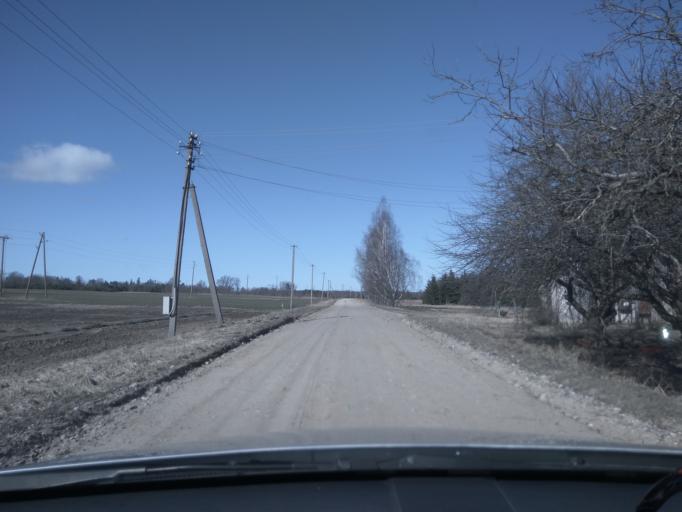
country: LV
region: Kuldigas Rajons
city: Kuldiga
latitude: 56.8928
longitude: 21.9704
